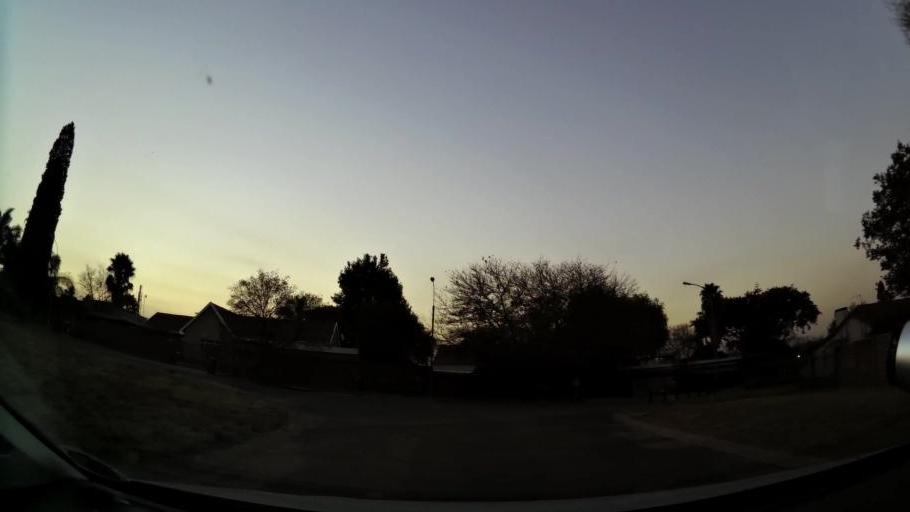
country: ZA
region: Gauteng
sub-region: Ekurhuleni Metropolitan Municipality
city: Tembisa
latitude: -26.0475
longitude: 28.2431
